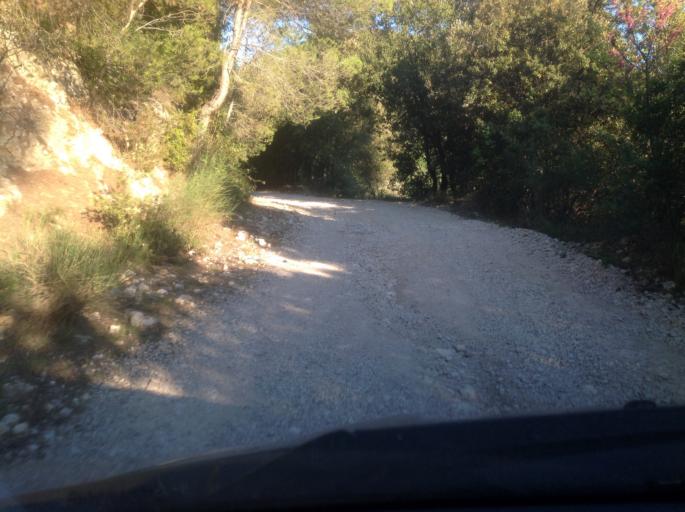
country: IT
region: Umbria
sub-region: Provincia di Terni
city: Stroncone
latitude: 42.5066
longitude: 12.6750
